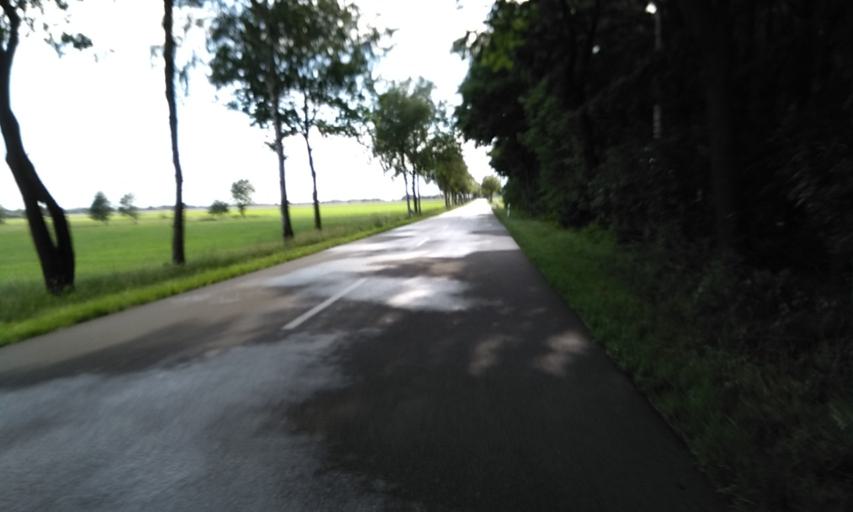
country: DE
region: Lower Saxony
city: Vierden
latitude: 53.3566
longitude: 9.4982
